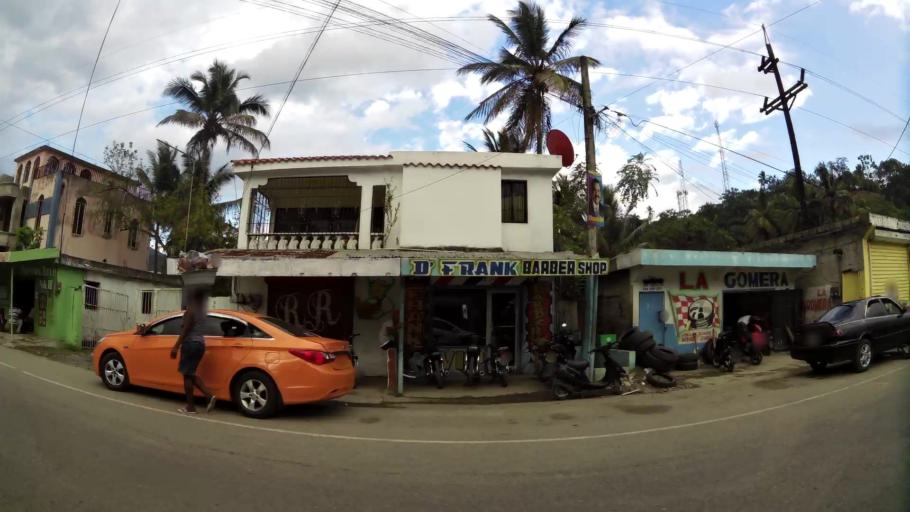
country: DO
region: San Cristobal
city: Villa Altagracia
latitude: 18.6794
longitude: -70.1775
